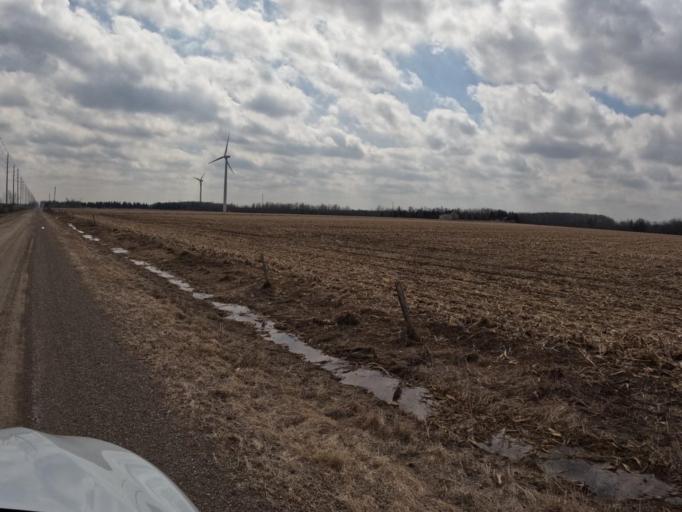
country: CA
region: Ontario
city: Shelburne
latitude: 44.0381
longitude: -80.3170
